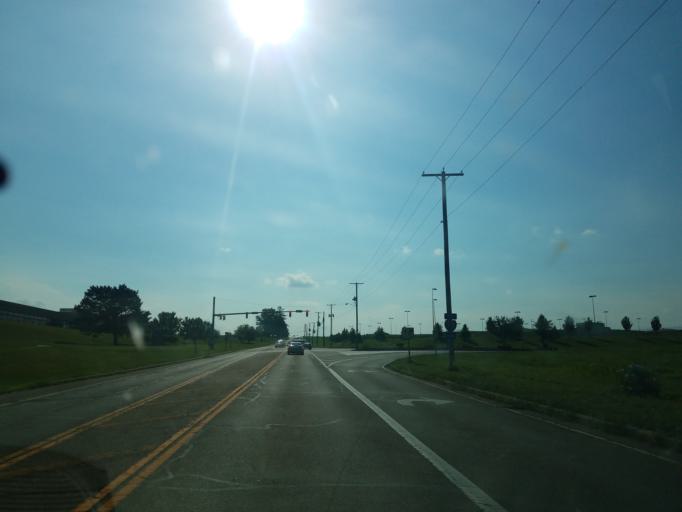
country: US
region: Ohio
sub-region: Stark County
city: Greentown
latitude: 40.9067
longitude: -81.4297
